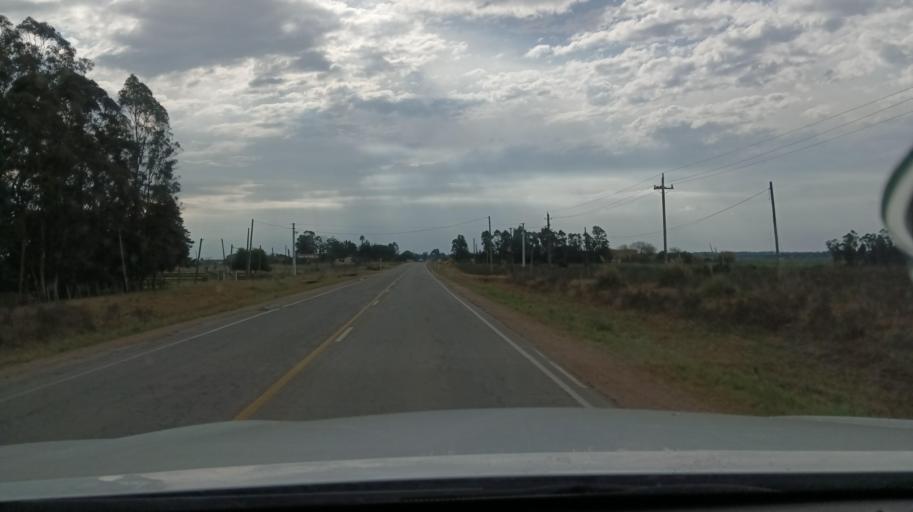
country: UY
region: Canelones
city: Toledo
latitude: -34.6981
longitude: -56.1062
